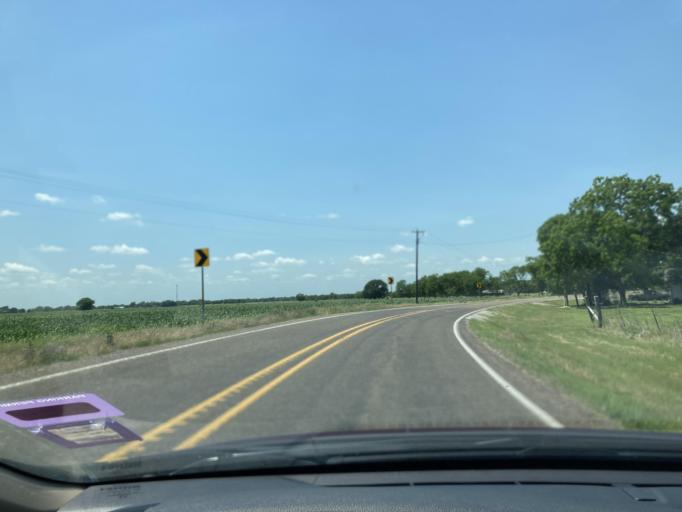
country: US
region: Texas
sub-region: Navarro County
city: Kerens
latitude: 32.1111
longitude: -96.3242
